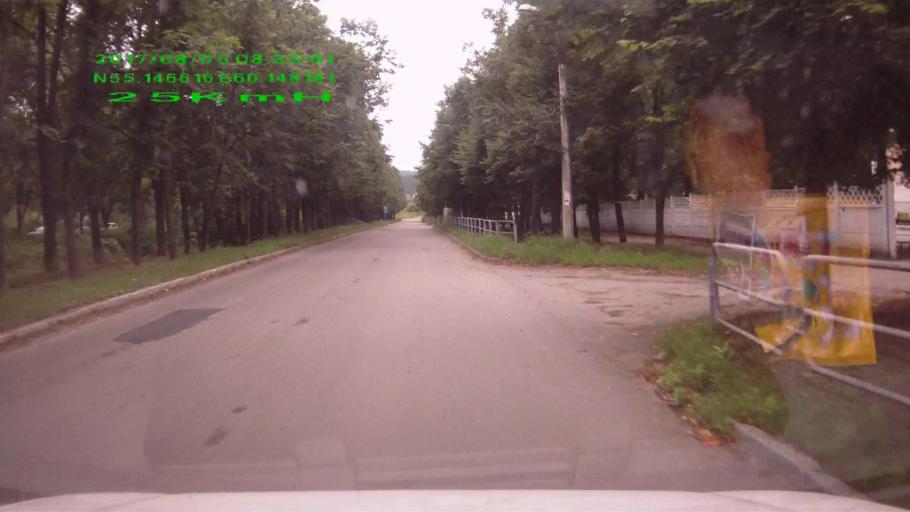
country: RU
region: Chelyabinsk
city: Turgoyak
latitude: 55.1467
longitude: 60.1480
